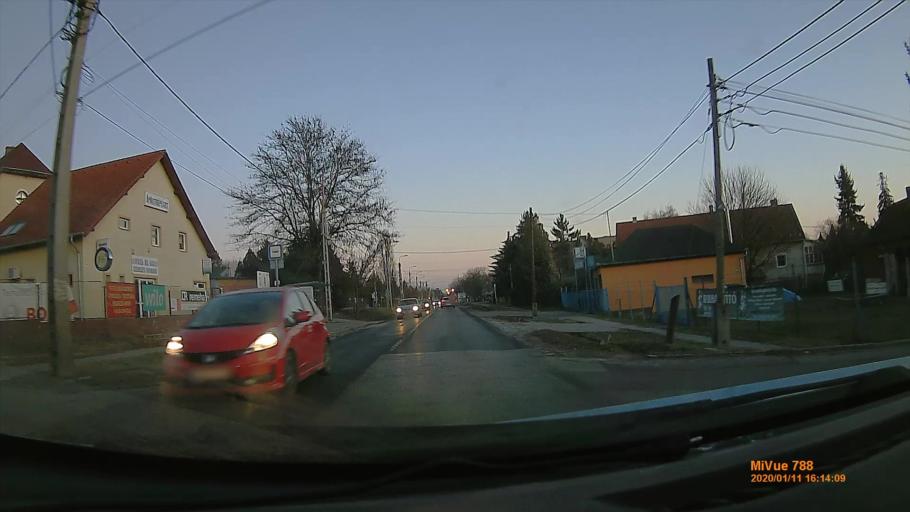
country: HU
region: Budapest
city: Budapest XVI. keruelet
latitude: 47.5332
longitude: 19.1854
